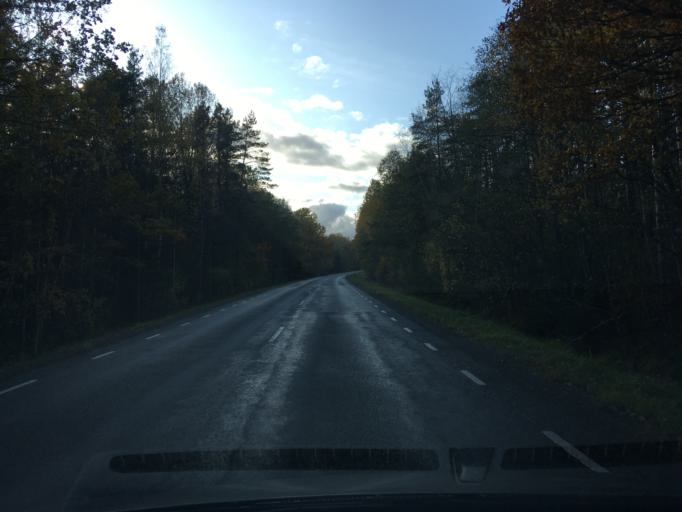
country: EE
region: Laeaene
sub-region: Lihula vald
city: Lihula
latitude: 58.5395
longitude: 23.9781
